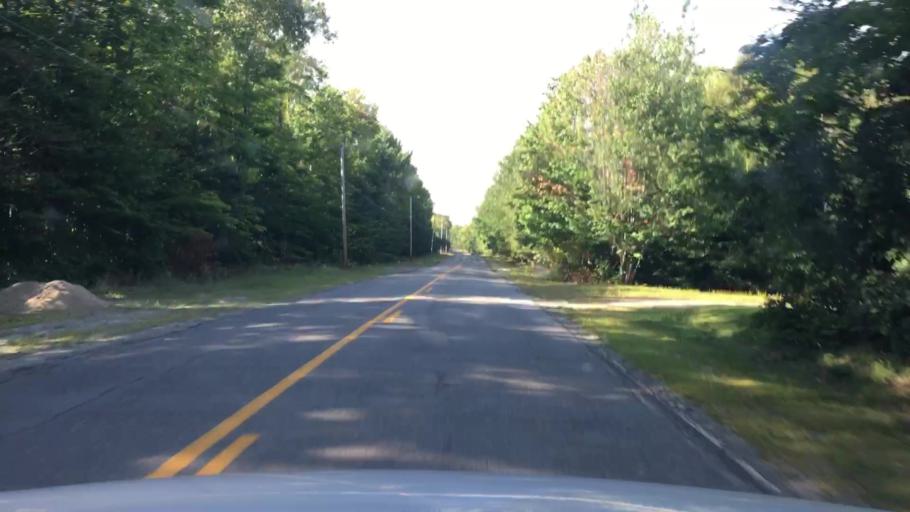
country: US
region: Maine
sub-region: Penobscot County
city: Enfield
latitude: 45.2199
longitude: -68.5360
